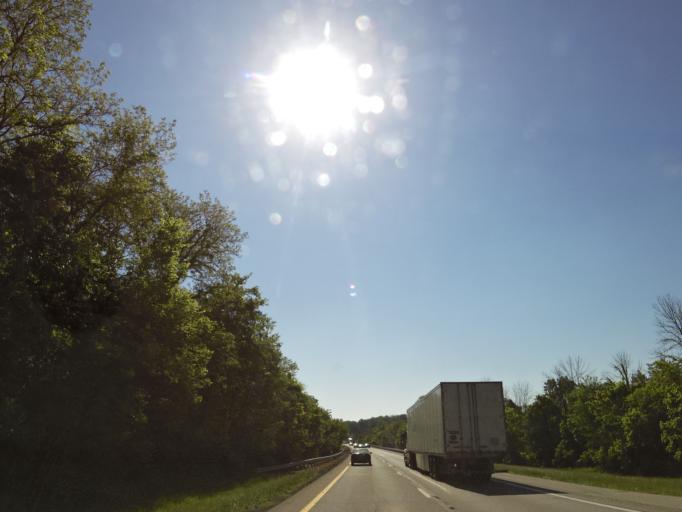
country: US
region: Kentucky
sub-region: Franklin County
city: Frankfort
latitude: 38.1487
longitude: -85.0384
